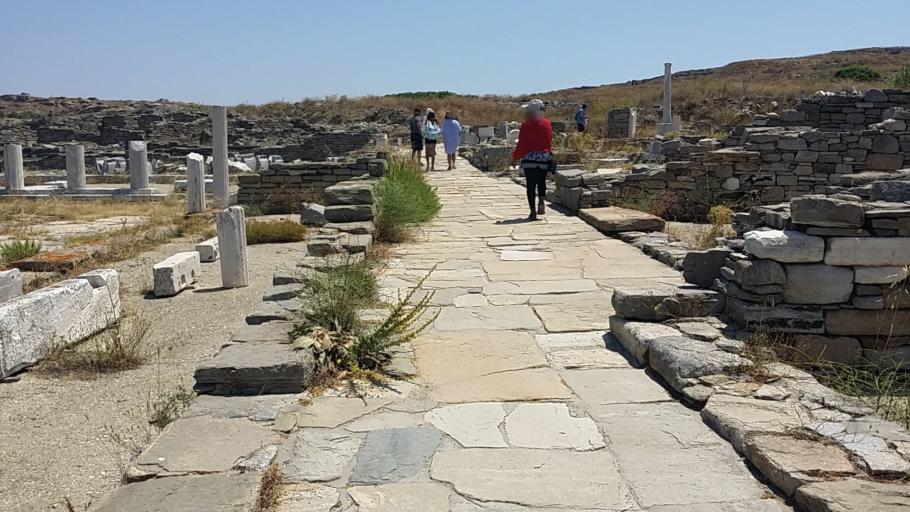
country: GR
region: South Aegean
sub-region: Nomos Kykladon
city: Mykonos
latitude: 37.3993
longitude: 25.2672
